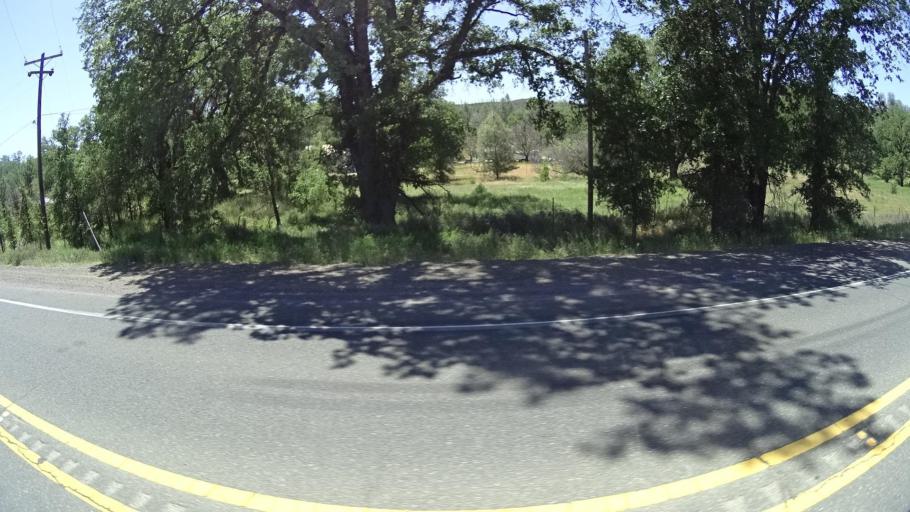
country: US
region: California
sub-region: Lake County
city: Lower Lake
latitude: 38.8479
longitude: -122.6112
